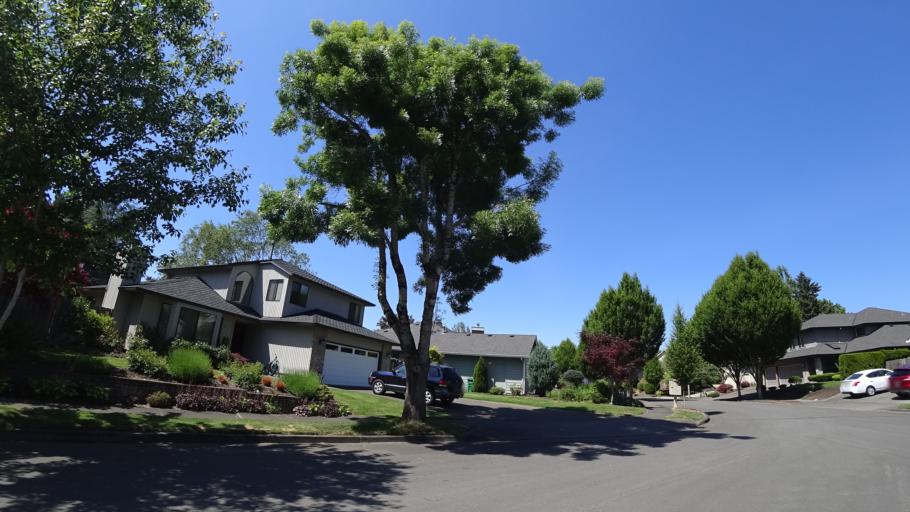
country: US
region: Oregon
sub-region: Washington County
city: King City
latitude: 45.4427
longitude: -122.8137
